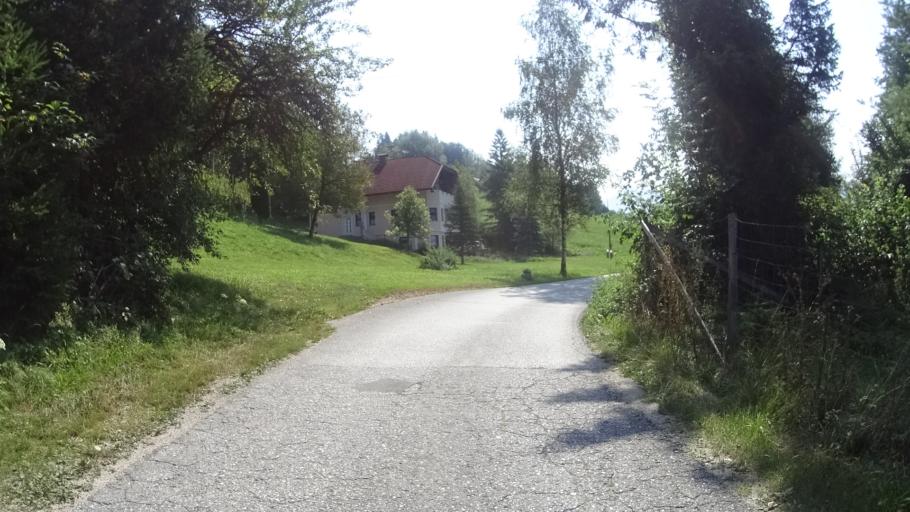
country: AT
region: Carinthia
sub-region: Politischer Bezirk Volkermarkt
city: Gallizien
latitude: 46.5681
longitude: 14.5296
